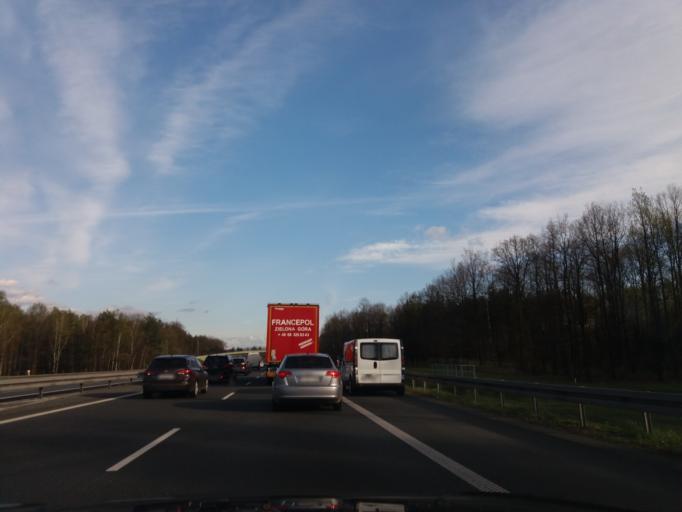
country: PL
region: Opole Voivodeship
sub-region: Powiat opolski
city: Niemodlin
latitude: 50.6880
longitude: 17.6347
